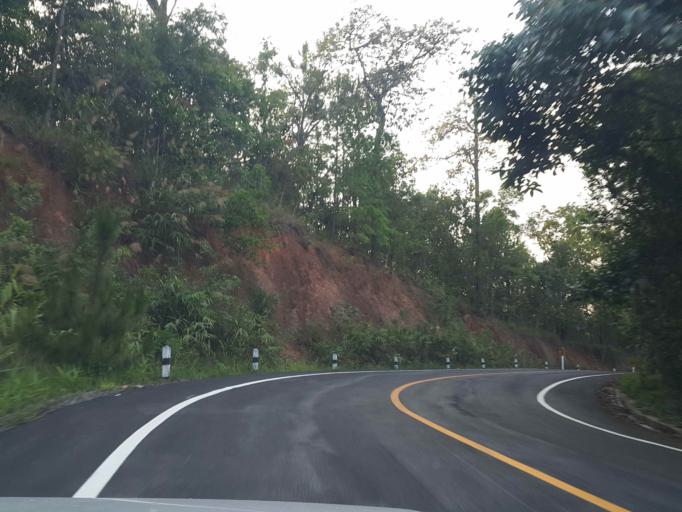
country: TH
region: Chiang Mai
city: Mae On
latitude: 19.0064
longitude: 99.3231
